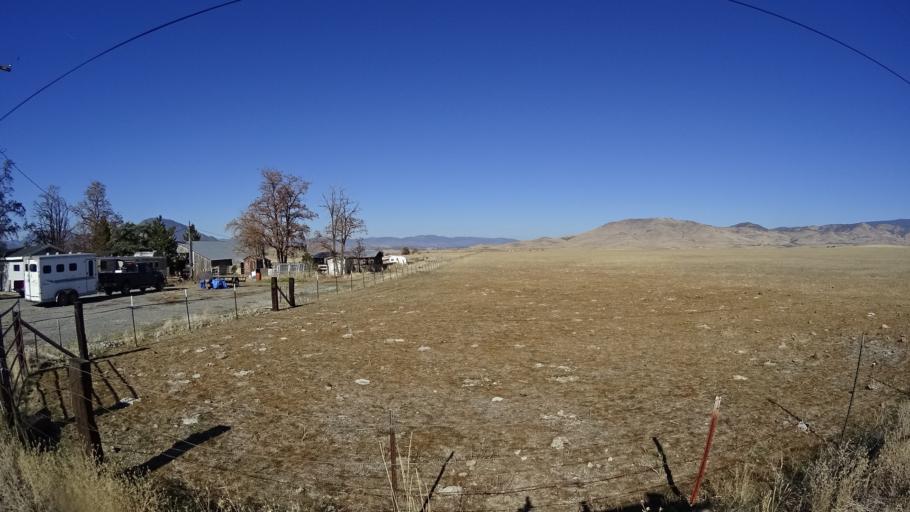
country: US
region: California
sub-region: Siskiyou County
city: Montague
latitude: 41.7937
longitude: -122.4301
